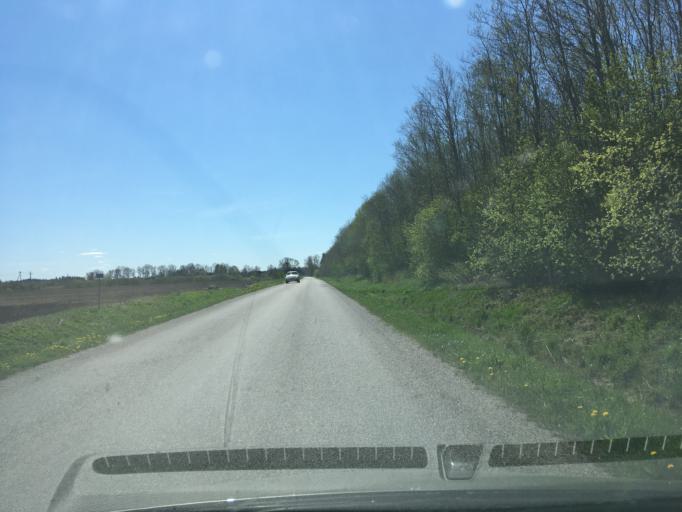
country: EE
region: Harju
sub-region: Raasiku vald
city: Arukula
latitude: 59.3974
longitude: 25.0798
